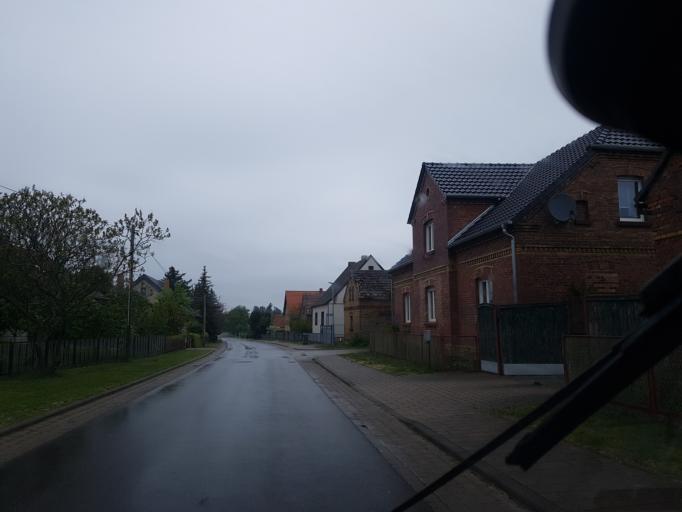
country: DE
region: Saxony
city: Gross Duben
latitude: 51.6707
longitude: 14.4722
